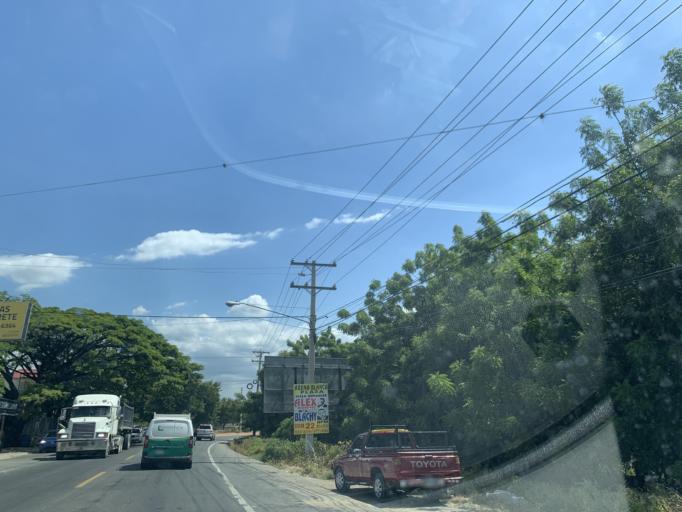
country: DO
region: Santiago
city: Villa Bisono
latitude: 19.5572
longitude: -70.8599
